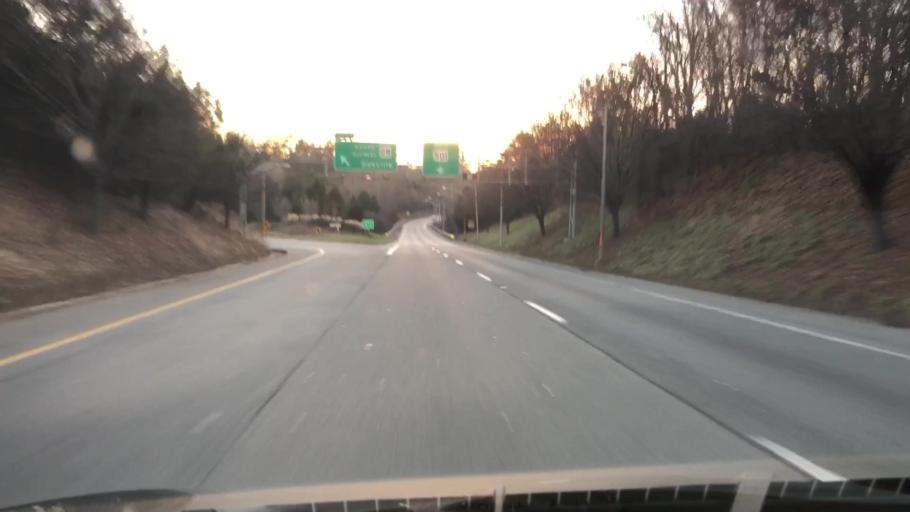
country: US
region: Virginia
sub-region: City of Lynchburg
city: West Lynchburg
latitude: 37.3651
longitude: -79.1836
